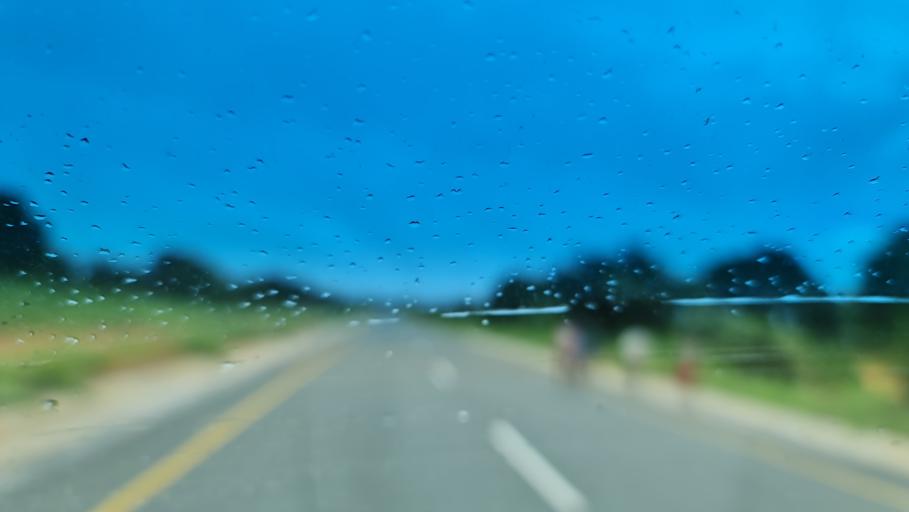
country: MZ
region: Nampula
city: Nampula
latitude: -15.5069
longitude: 39.3331
